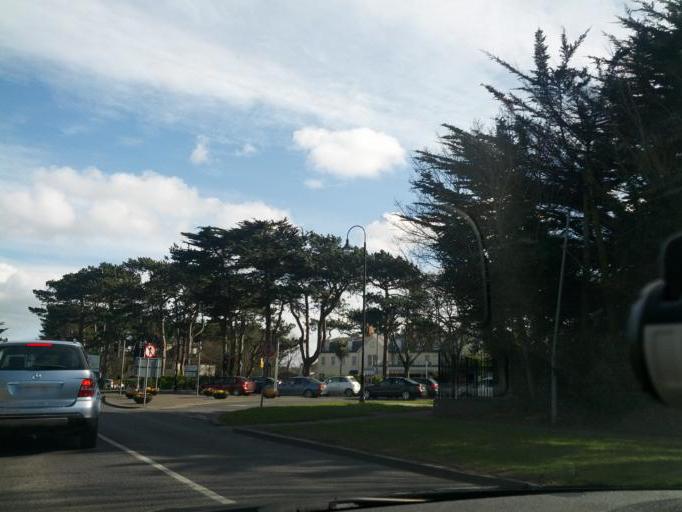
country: IE
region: Leinster
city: Sutton
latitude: 53.3898
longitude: -6.1112
